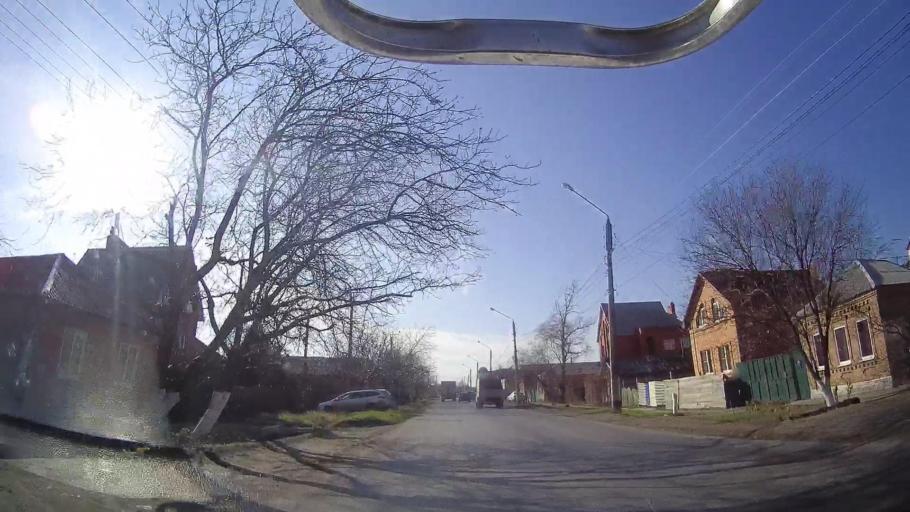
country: RU
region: Rostov
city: Bataysk
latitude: 47.1284
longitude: 39.6949
